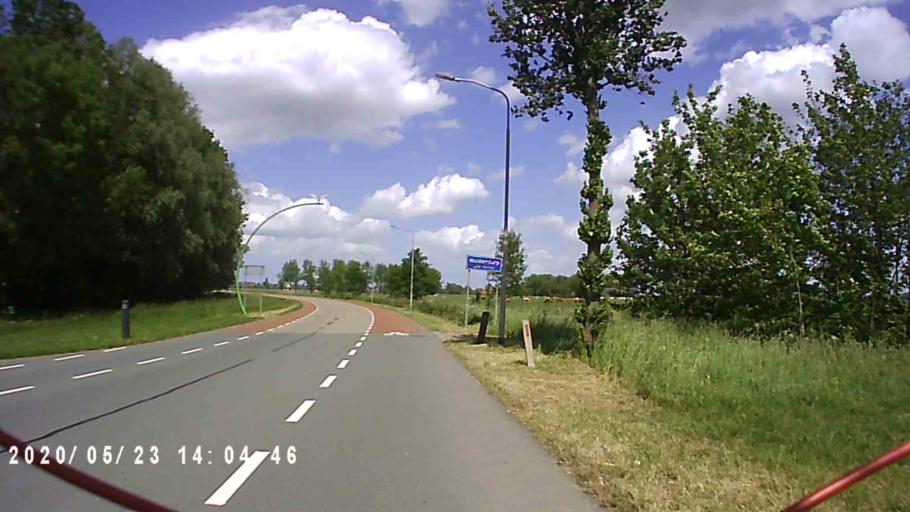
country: NL
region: Groningen
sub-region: Gemeente Delfzijl
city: Delfzijl
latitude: 53.2784
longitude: 7.0346
